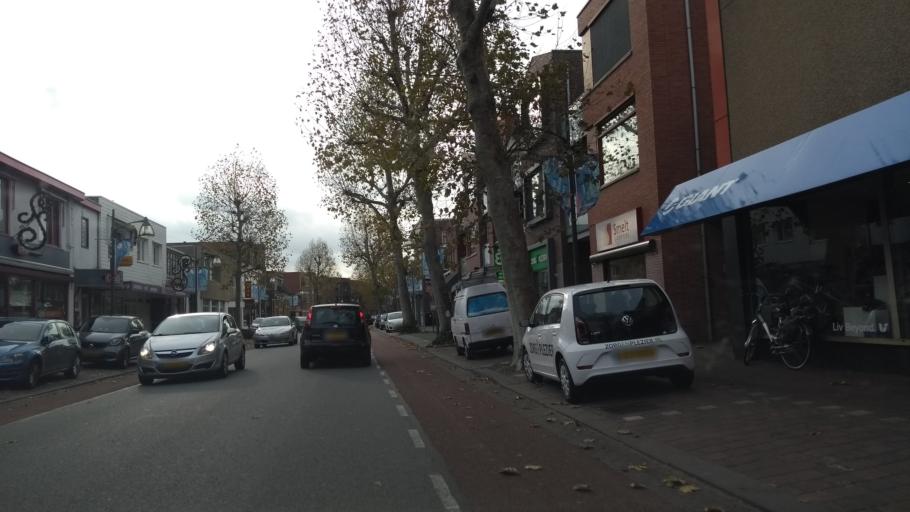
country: NL
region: Overijssel
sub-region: Gemeente Almelo
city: Almelo
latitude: 52.3681
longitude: 6.6826
